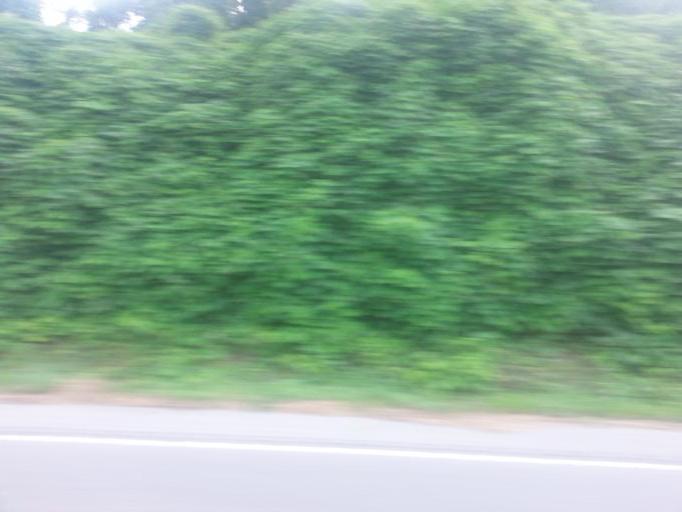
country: US
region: Tennessee
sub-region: Sevier County
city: Seymour
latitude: 35.8638
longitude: -83.6563
